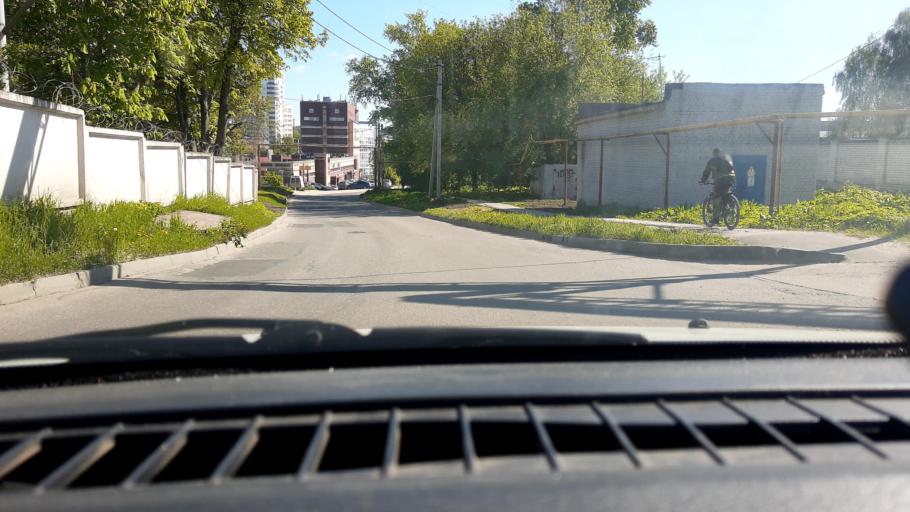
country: RU
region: Nizjnij Novgorod
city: Nizhniy Novgorod
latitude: 56.3039
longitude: 44.0161
